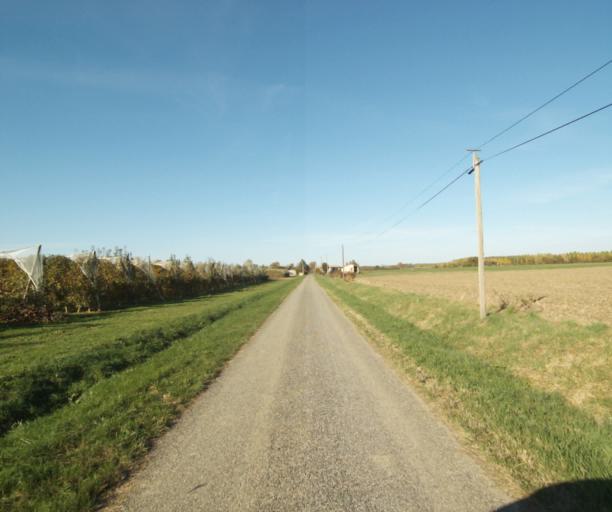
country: FR
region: Midi-Pyrenees
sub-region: Departement du Tarn-et-Garonne
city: Finhan
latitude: 43.9316
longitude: 1.2062
